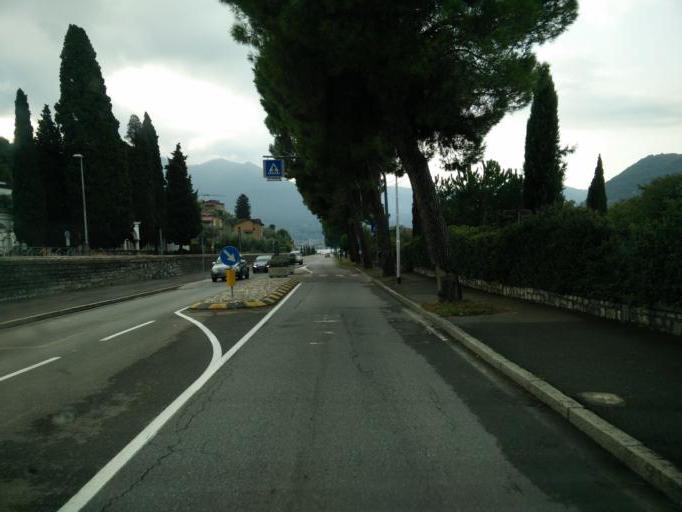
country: IT
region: Lombardy
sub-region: Provincia di Brescia
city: Marone
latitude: 45.7323
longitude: 10.0933
